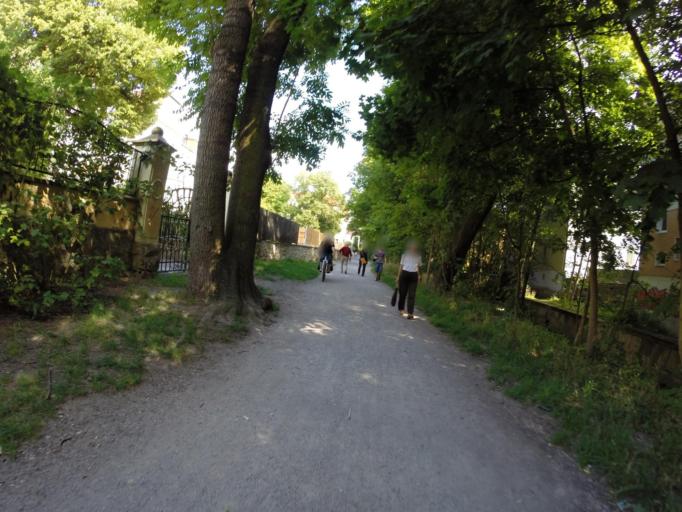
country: DE
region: Thuringia
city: Jena
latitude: 50.9311
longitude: 11.5730
